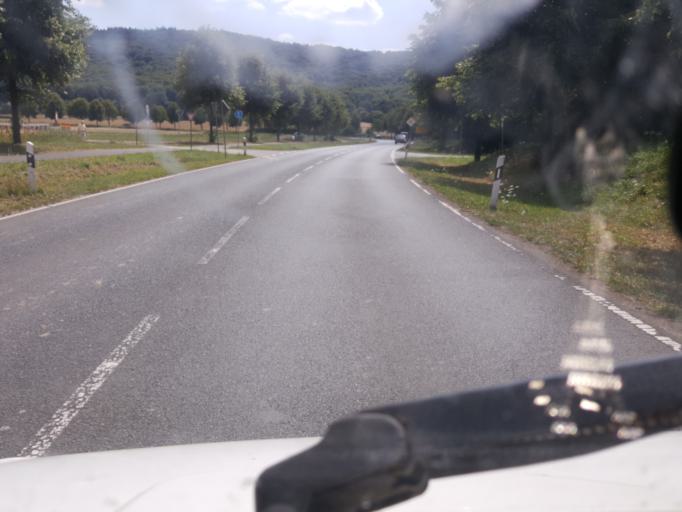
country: DE
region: North Rhine-Westphalia
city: Porta Westfalica
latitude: 52.2593
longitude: 8.8931
